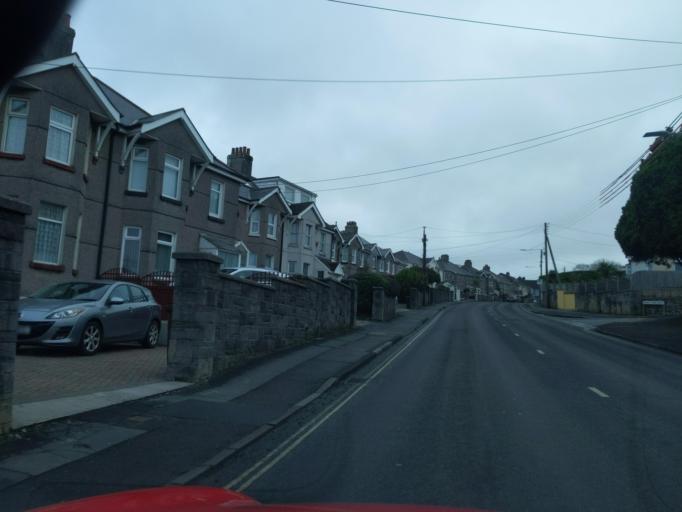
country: GB
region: England
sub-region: Plymouth
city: Plymstock
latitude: 50.3592
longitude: -4.0916
